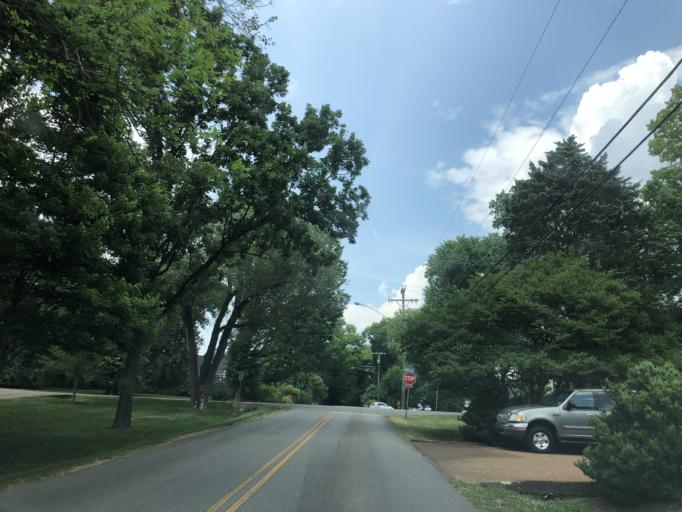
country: US
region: Tennessee
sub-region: Davidson County
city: Oak Hill
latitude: 36.1161
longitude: -86.8157
